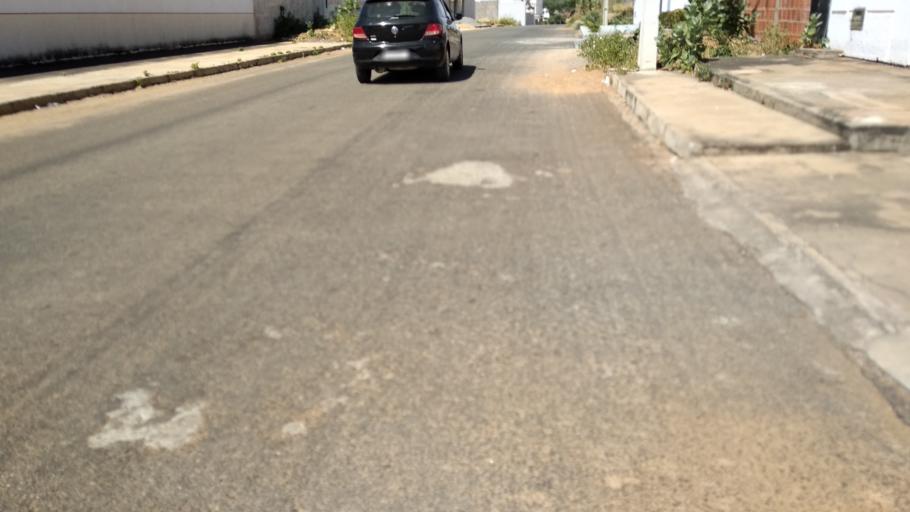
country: BR
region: Bahia
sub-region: Guanambi
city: Guanambi
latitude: -14.2280
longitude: -42.7749
